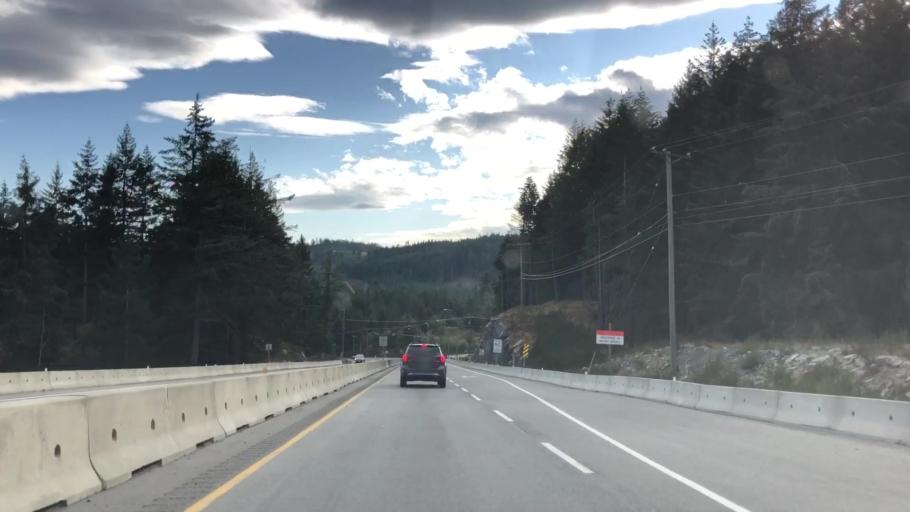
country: CA
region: British Columbia
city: Langford
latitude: 48.5631
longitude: -123.5667
